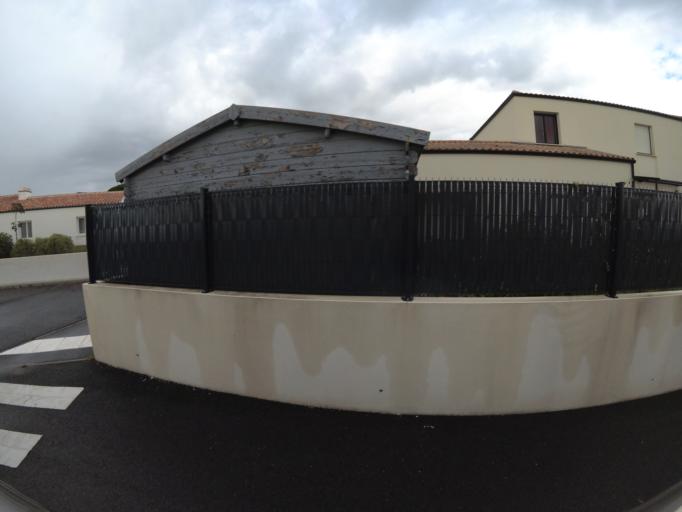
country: FR
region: Pays de la Loire
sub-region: Departement de la Loire-Atlantique
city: Saint-Hilaire-de-Clisson
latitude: 47.0663
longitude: -1.3110
